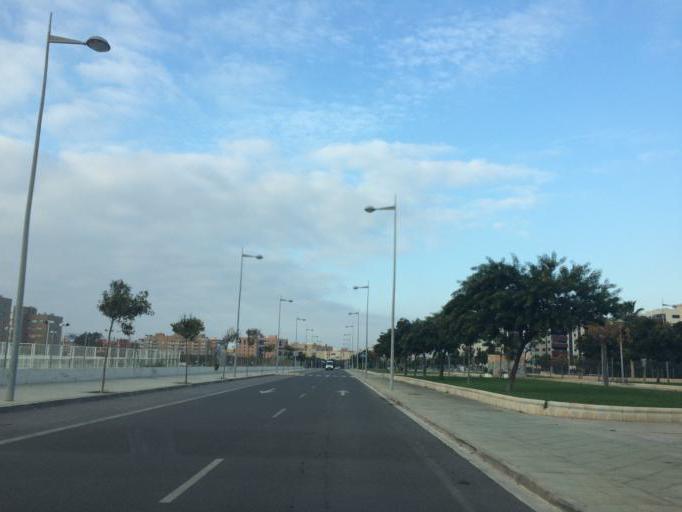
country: ES
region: Andalusia
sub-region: Provincia de Almeria
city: Almeria
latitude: 36.8298
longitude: -2.4402
